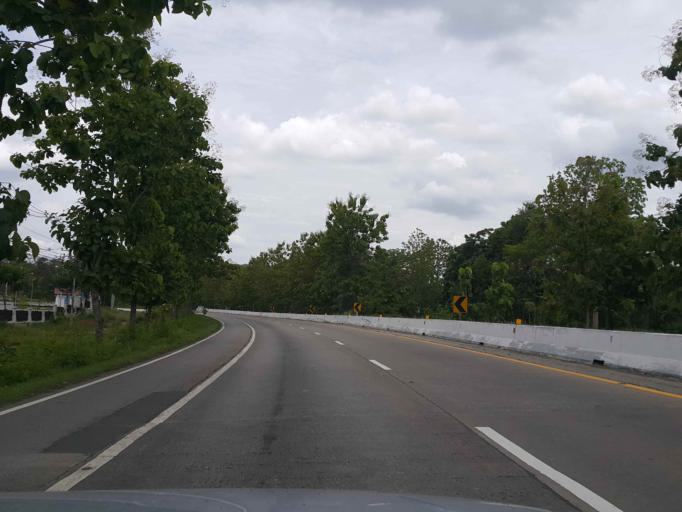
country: TH
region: Lamphun
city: Mae Tha
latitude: 18.5090
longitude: 99.0993
